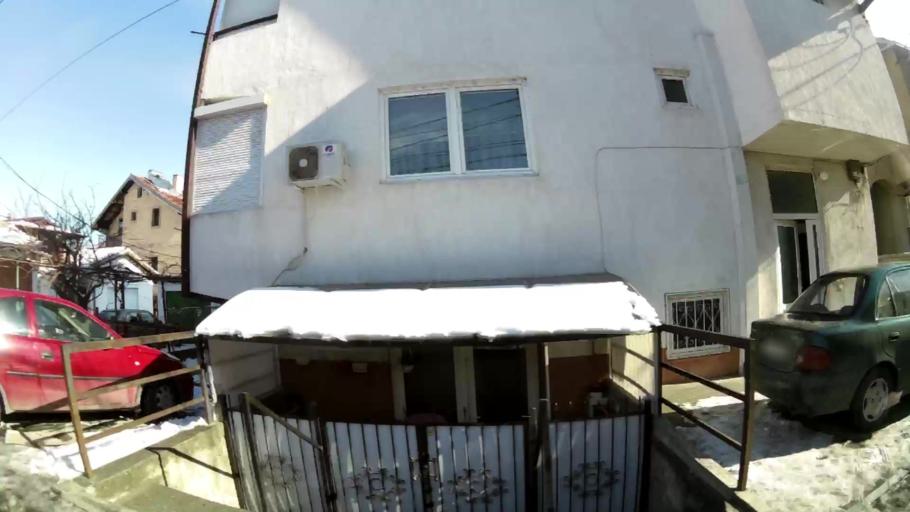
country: MK
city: Krushopek
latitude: 42.0081
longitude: 21.3579
